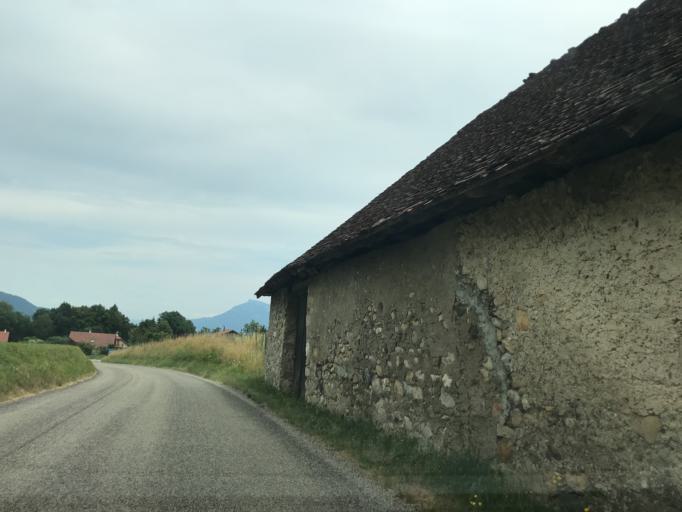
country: FR
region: Rhone-Alpes
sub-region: Departement de l'Isere
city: Chapareillan
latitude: 45.4666
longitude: 5.9666
